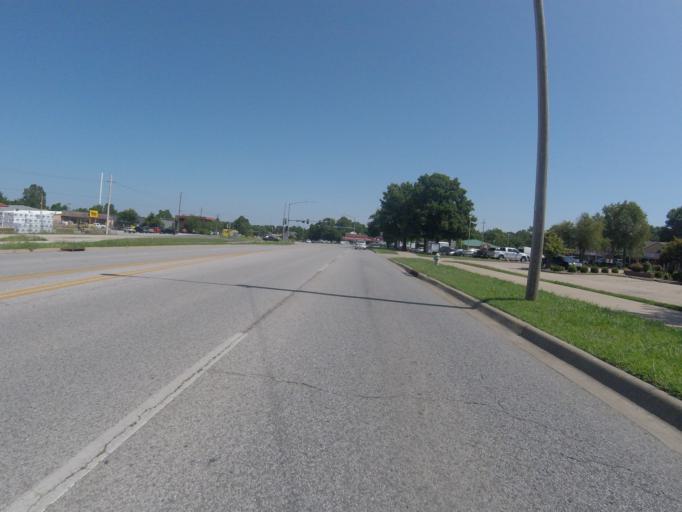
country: US
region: Arkansas
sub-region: Washington County
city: Fayetteville
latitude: 36.0944
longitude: -94.1608
